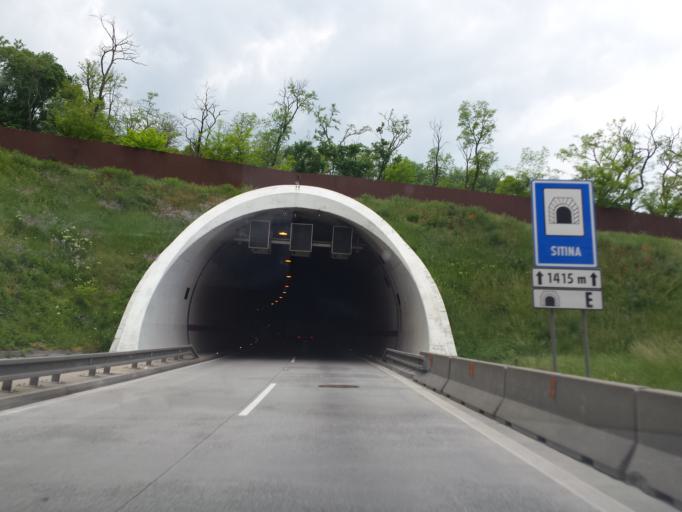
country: SK
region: Bratislavsky
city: Bratislava
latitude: 48.1636
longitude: 17.0745
